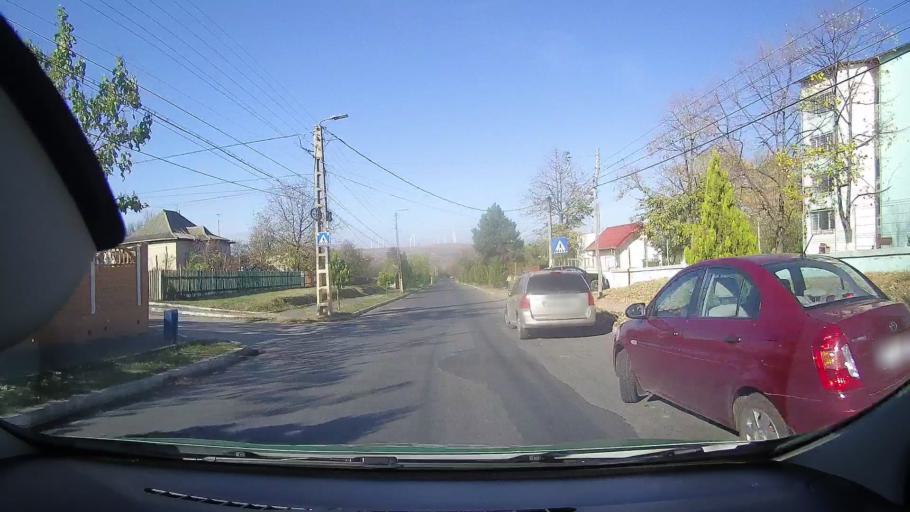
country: RO
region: Tulcea
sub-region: Oras Babadag
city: Babadag
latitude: 44.8878
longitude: 28.7323
